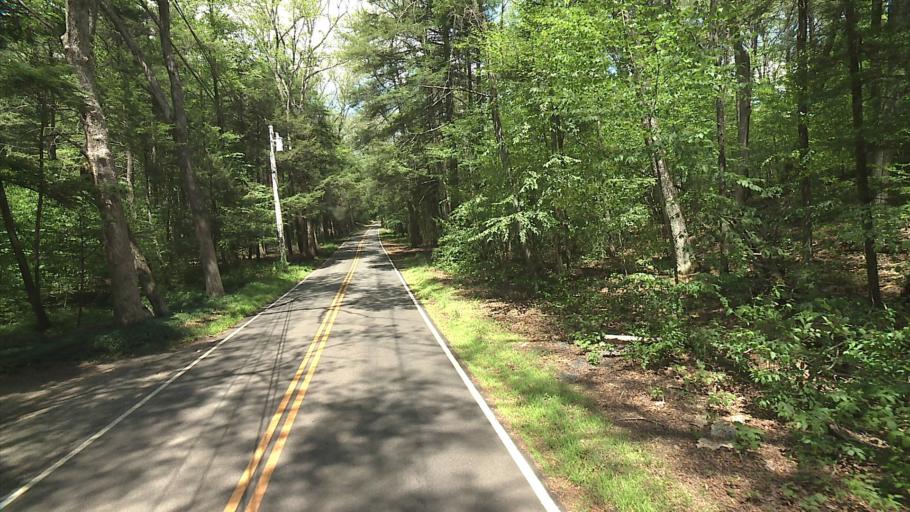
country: US
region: Connecticut
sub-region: Middlesex County
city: Essex Village
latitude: 41.4554
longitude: -72.3382
